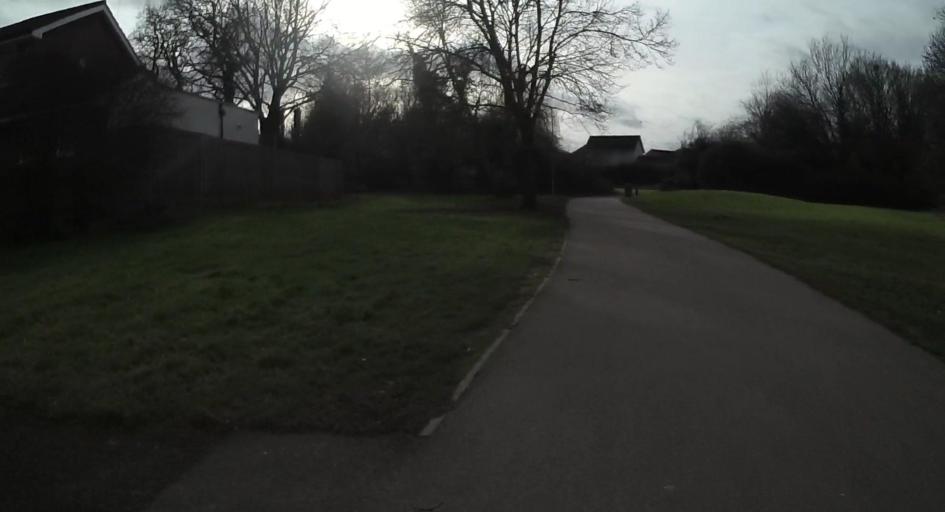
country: GB
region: England
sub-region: Wokingham
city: Wokingham
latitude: 51.4107
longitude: -0.8535
